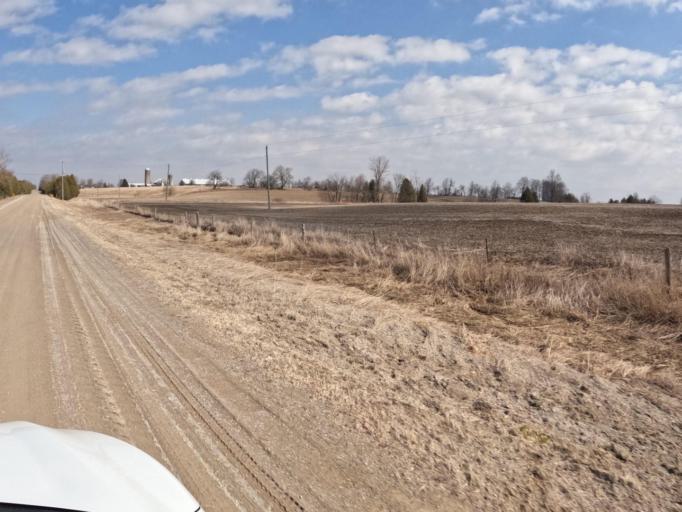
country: CA
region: Ontario
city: Orangeville
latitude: 43.9191
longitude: -80.2551
